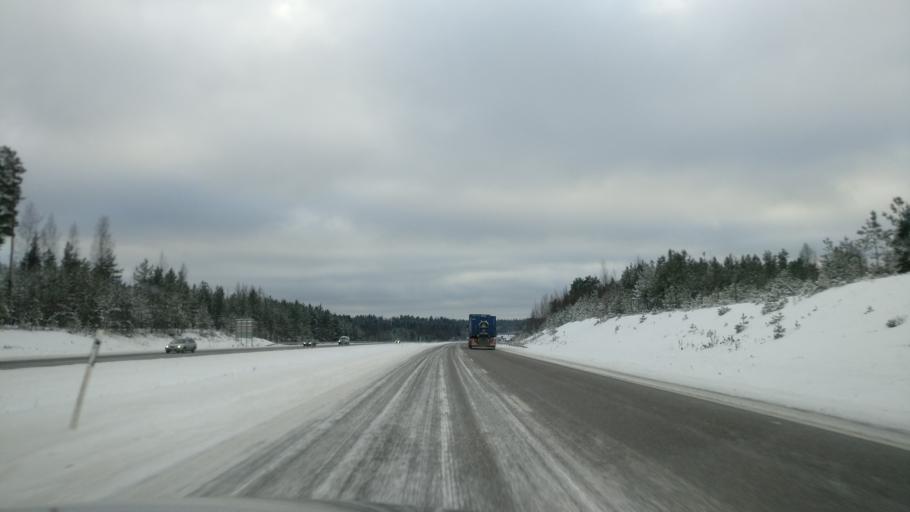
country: FI
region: Paijanne Tavastia
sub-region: Lahti
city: Nastola
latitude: 61.1043
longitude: 25.9132
